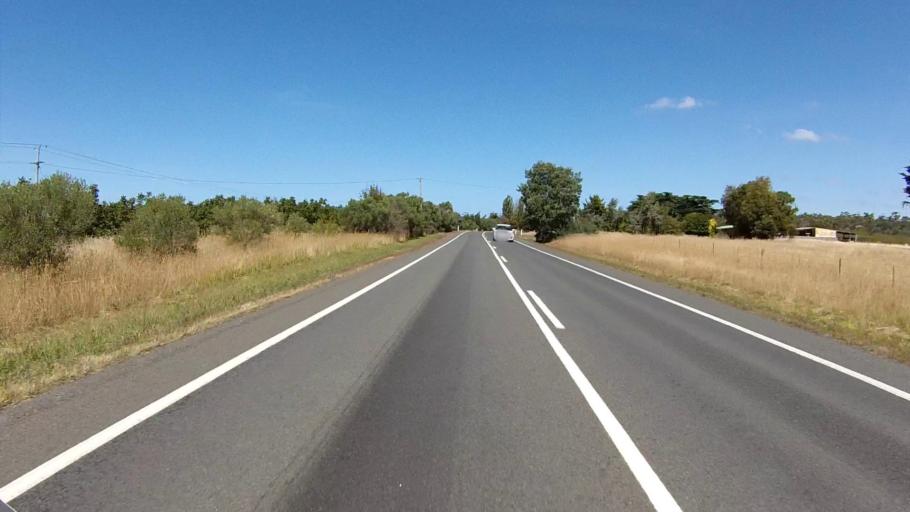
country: AU
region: Tasmania
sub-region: Break O'Day
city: St Helens
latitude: -42.0718
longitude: 148.0665
